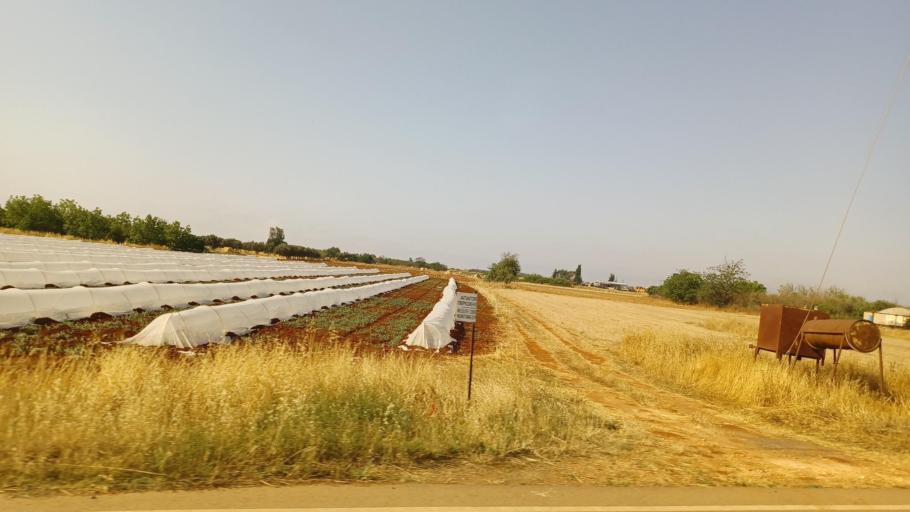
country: CY
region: Ammochostos
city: Liopetri
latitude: 35.0418
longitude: 33.8783
